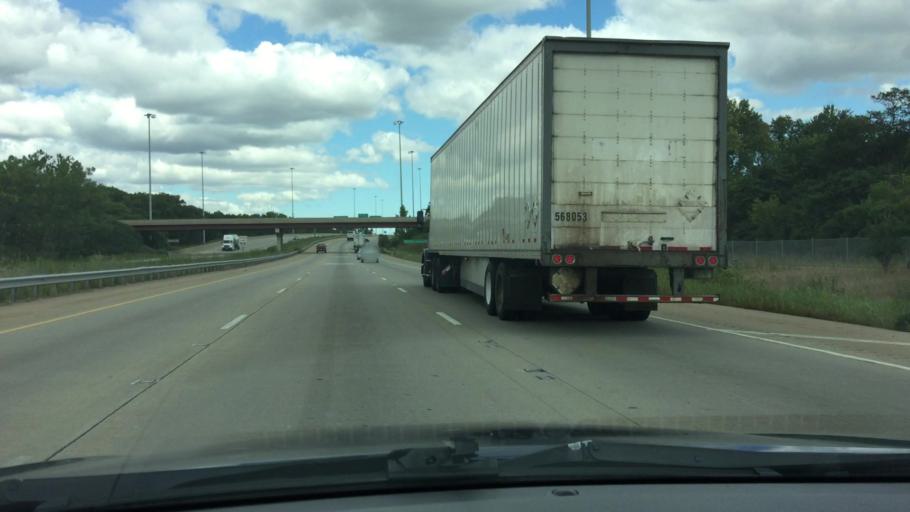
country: US
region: Illinois
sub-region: Cook County
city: Thornton
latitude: 41.5687
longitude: -87.5835
